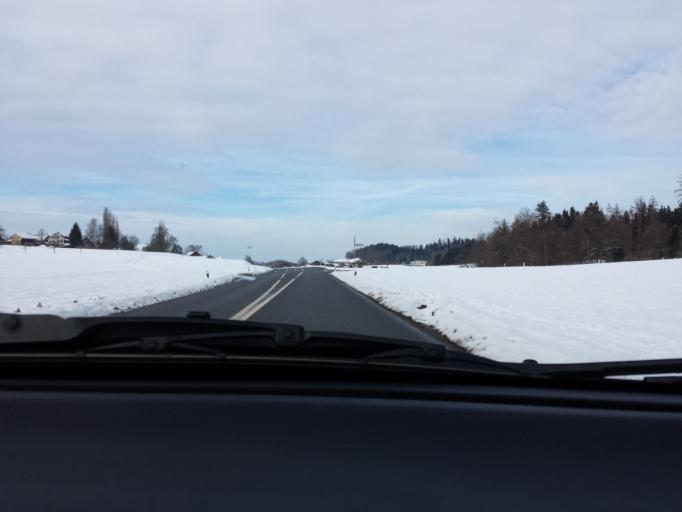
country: CH
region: Zurich
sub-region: Bezirk Hinwil
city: Bubikon
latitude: 47.2817
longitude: 8.8091
